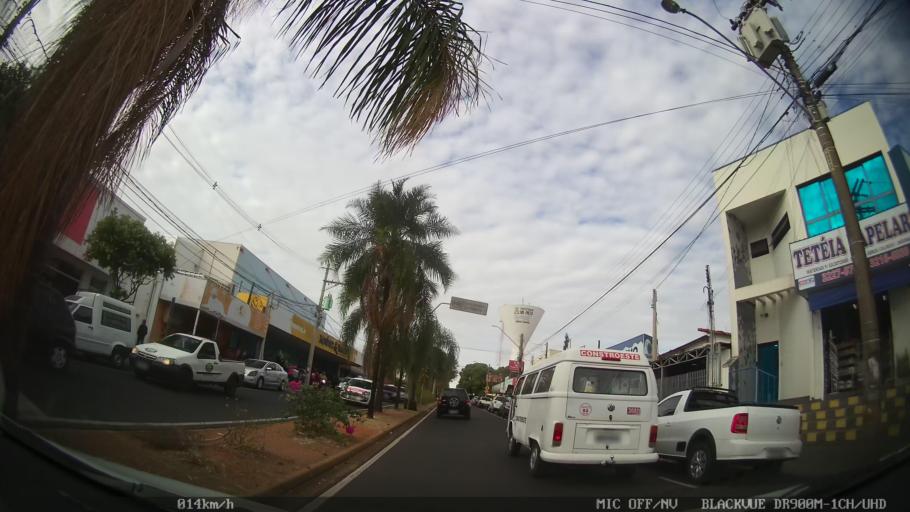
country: BR
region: Sao Paulo
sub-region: Sao Jose Do Rio Preto
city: Sao Jose do Rio Preto
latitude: -20.8285
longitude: -49.3730
